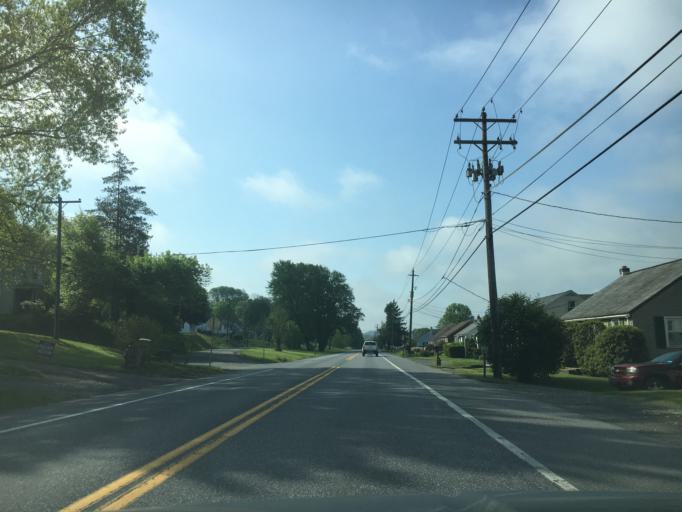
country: US
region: Pennsylvania
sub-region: Berks County
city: Boyertown
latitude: 40.3479
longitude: -75.6616
